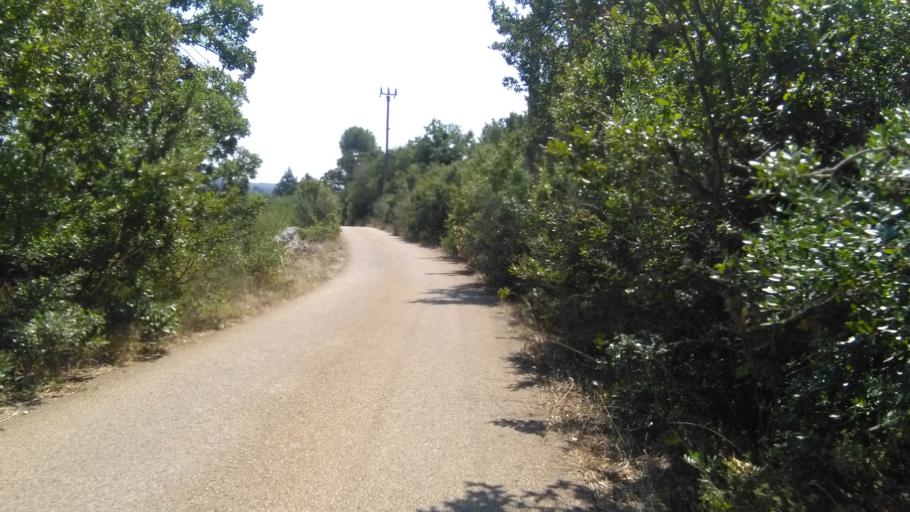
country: IT
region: Apulia
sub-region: Provincia di Bari
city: Noci
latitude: 40.8180
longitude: 17.1528
